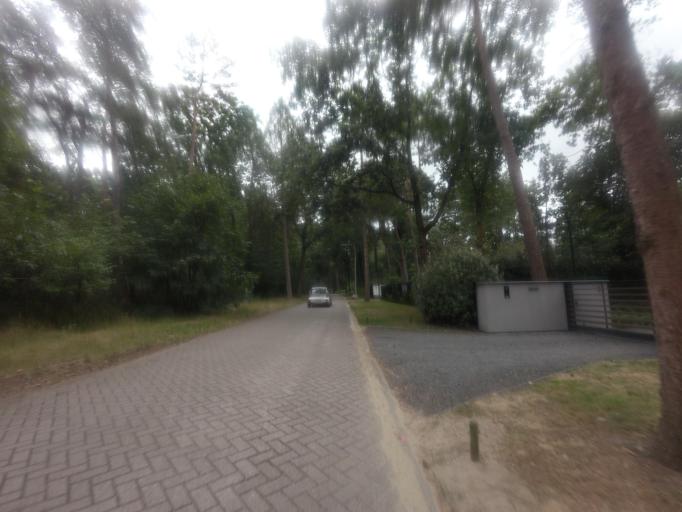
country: NL
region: Utrecht
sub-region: Gemeente Zeist
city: Zeist
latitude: 52.1335
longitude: 5.2443
